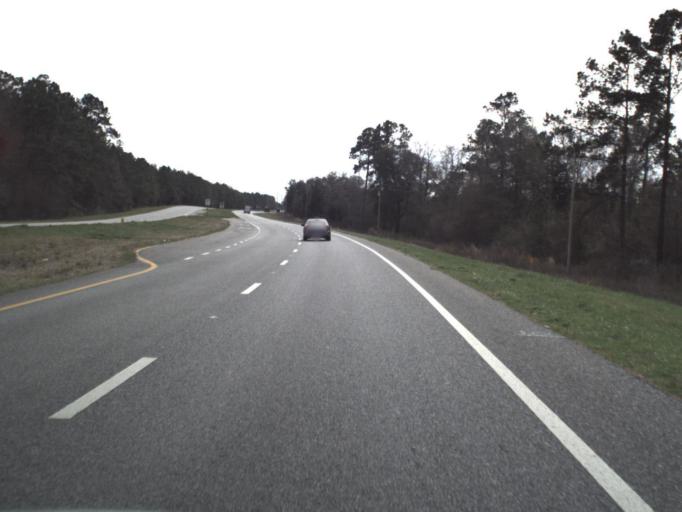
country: US
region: Florida
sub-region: Washington County
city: Chipley
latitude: 30.7452
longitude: -85.3852
